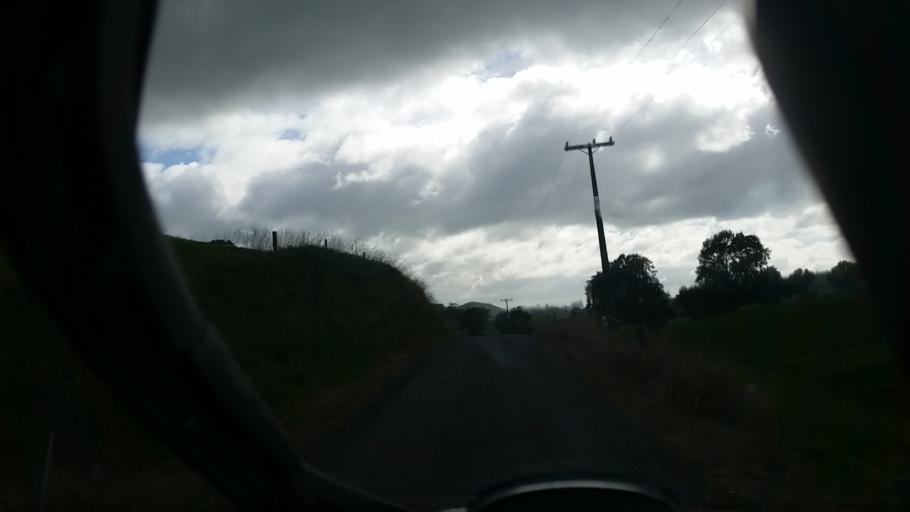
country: NZ
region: Waikato
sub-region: Matamata-Piako District
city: Matamata
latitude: -37.8181
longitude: 175.6744
